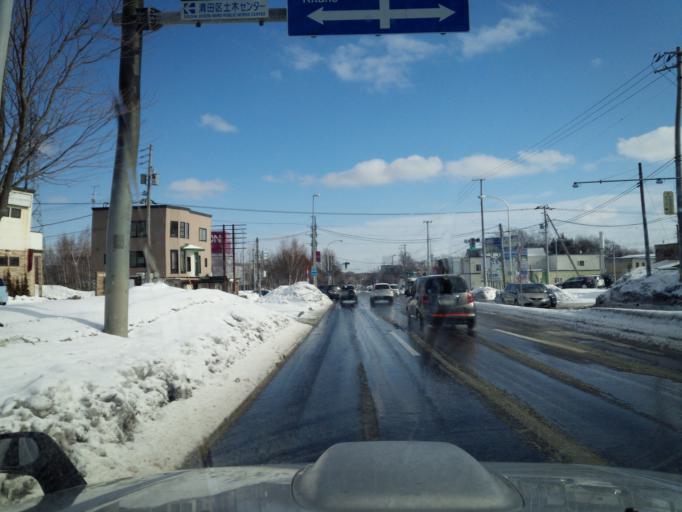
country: JP
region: Hokkaido
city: Kitahiroshima
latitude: 42.9939
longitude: 141.4566
